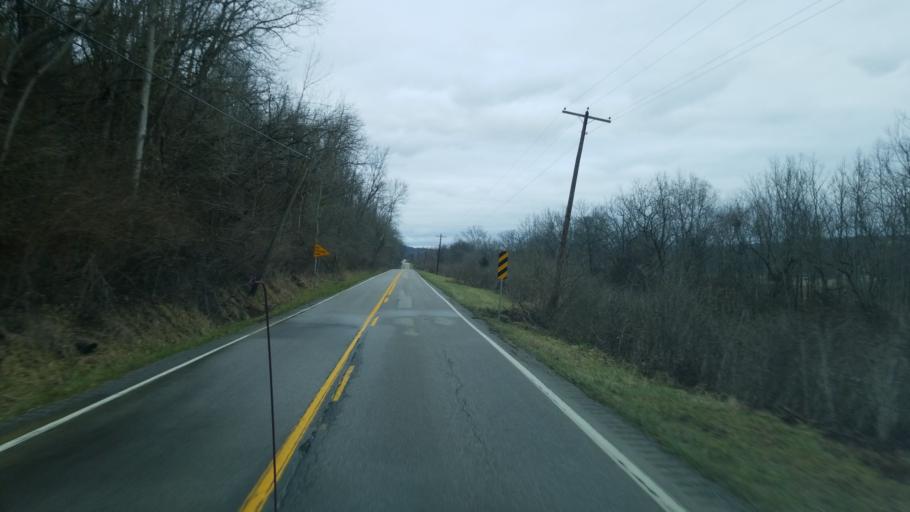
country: US
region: Ohio
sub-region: Clermont County
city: New Richmond
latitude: 38.9234
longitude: -84.2712
